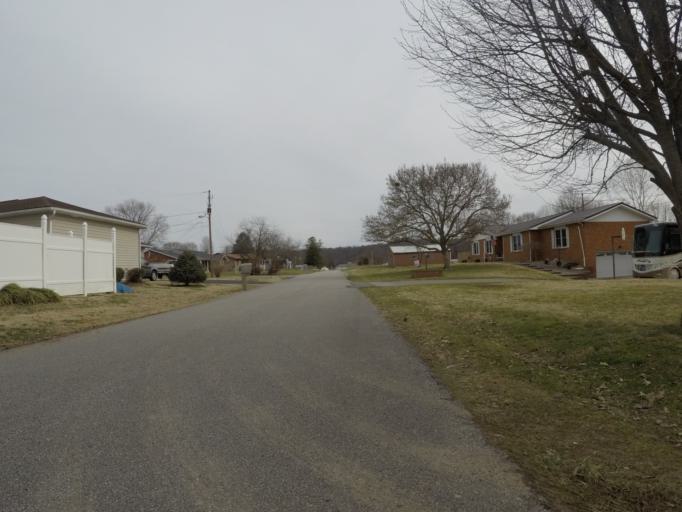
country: US
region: West Virginia
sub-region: Cabell County
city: Pea Ridge
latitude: 38.4501
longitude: -82.3320
